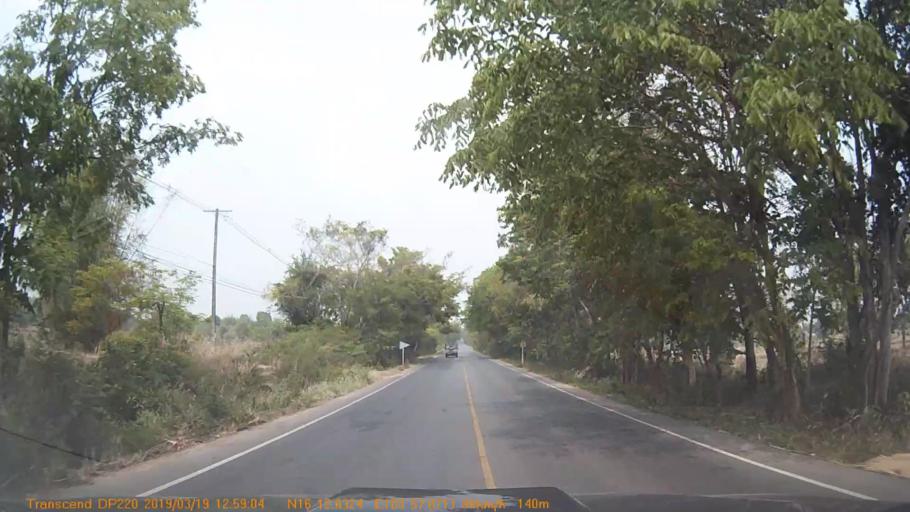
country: TH
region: Roi Et
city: Waeng
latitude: 16.2108
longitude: 103.9513
